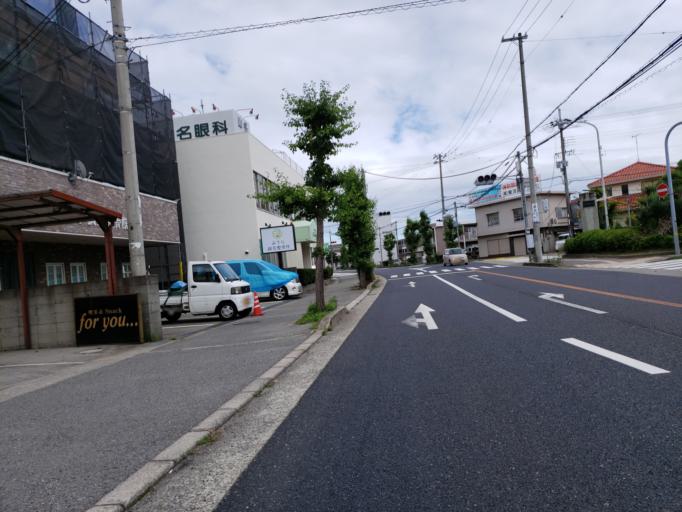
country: JP
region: Hyogo
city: Kakogawacho-honmachi
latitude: 34.7661
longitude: 134.7916
